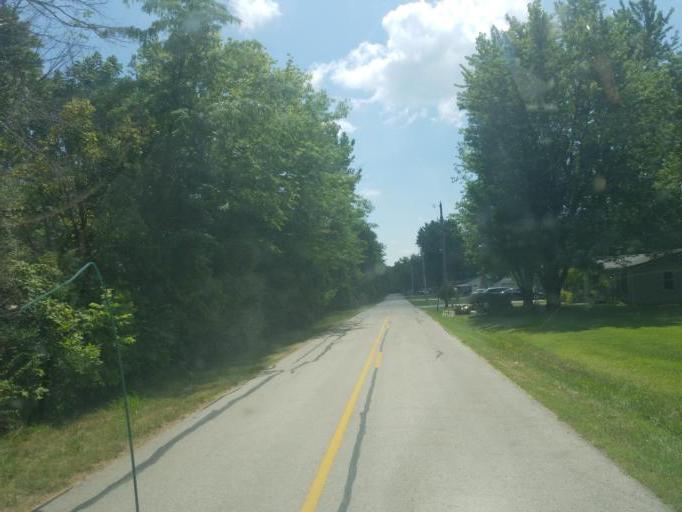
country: US
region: Ohio
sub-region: Auglaize County
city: Saint Marys
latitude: 40.5502
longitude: -84.4445
